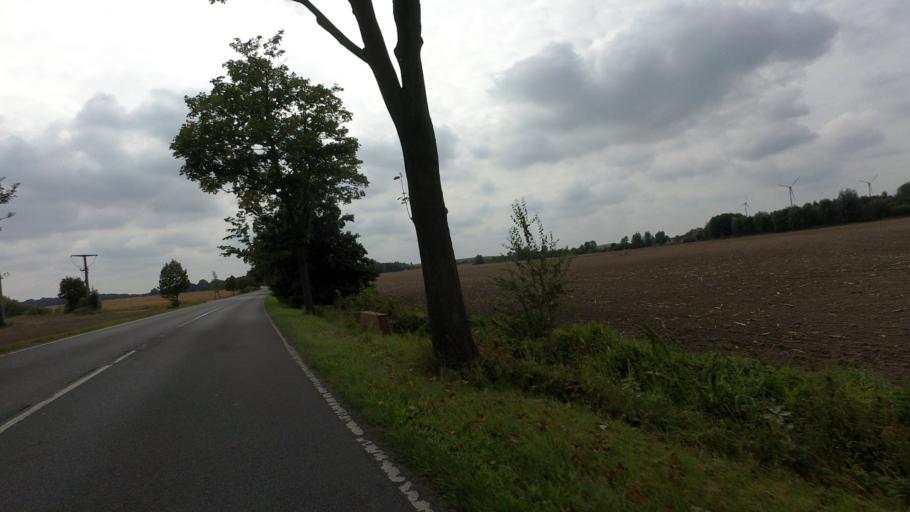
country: DE
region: Brandenburg
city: Luckau
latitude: 51.8386
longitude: 13.6892
